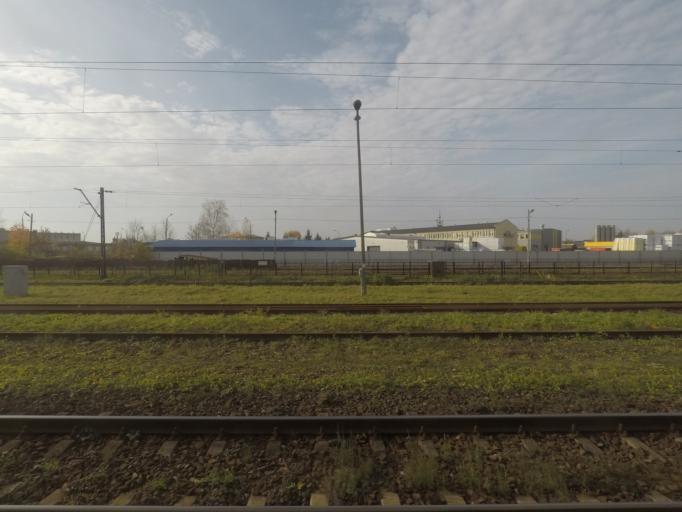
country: PL
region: Subcarpathian Voivodeship
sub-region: Rzeszow
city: Rzeszow
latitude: 50.0496
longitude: 21.9948
